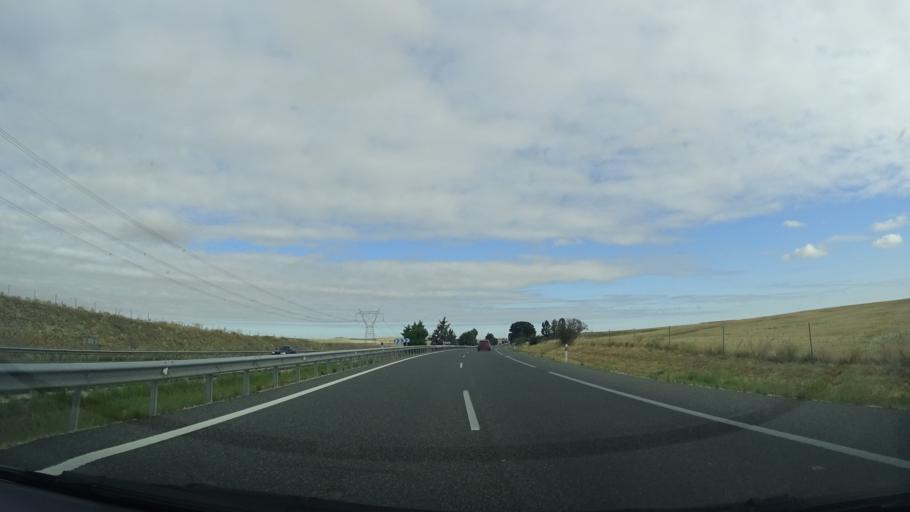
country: ES
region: Castille and Leon
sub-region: Provincia de Valladolid
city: San Pablo de la Moraleja
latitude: 41.1576
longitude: -4.7955
